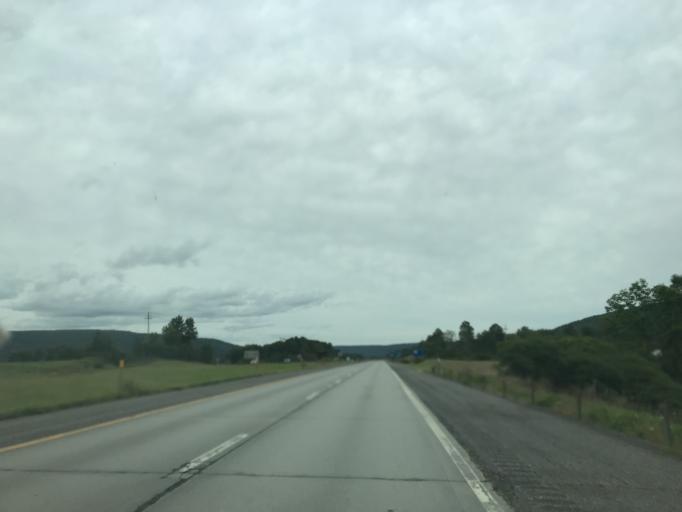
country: US
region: New York
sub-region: Otsego County
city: Oneonta
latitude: 42.4777
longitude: -74.9846
